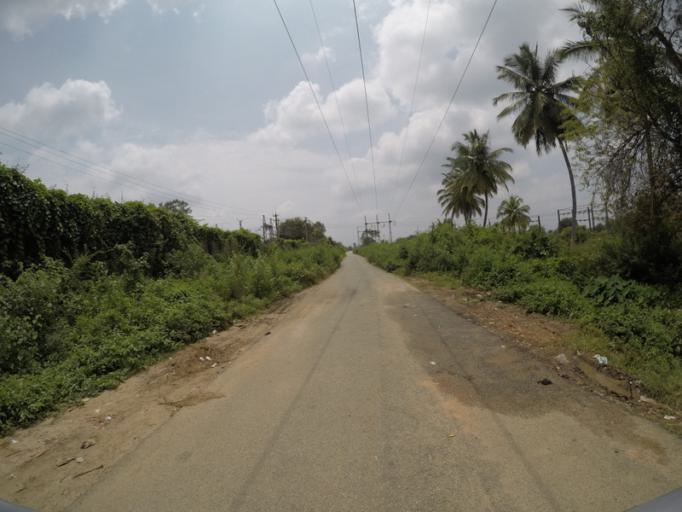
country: IN
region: Karnataka
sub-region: Ramanagara
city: Kanakapura
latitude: 12.6708
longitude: 77.4543
